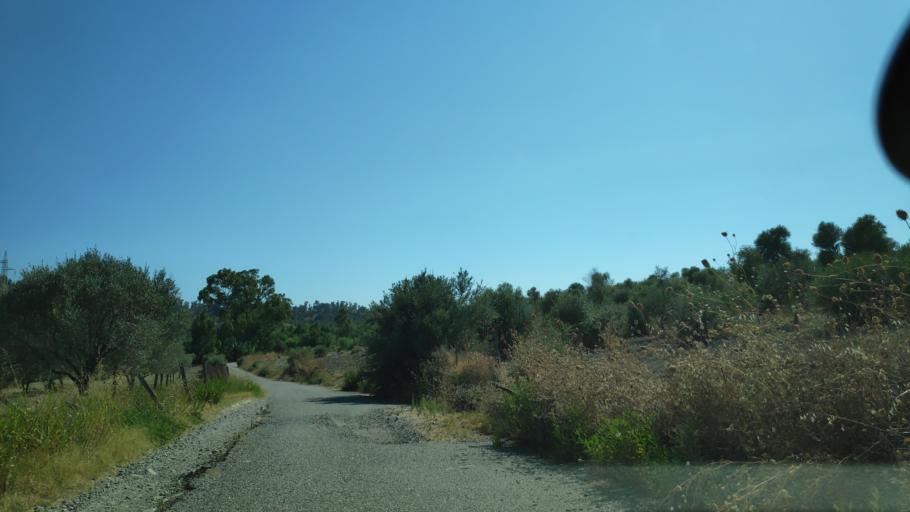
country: IT
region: Calabria
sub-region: Provincia di Reggio Calabria
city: Monasterace
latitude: 38.4299
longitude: 16.5244
